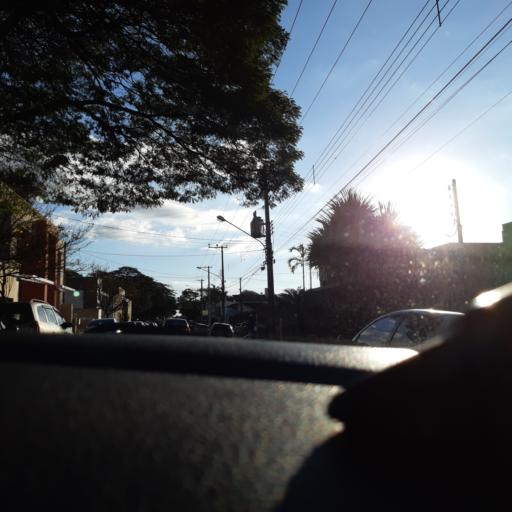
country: BR
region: Sao Paulo
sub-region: Ourinhos
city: Ourinhos
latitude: -22.9826
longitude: -49.8624
